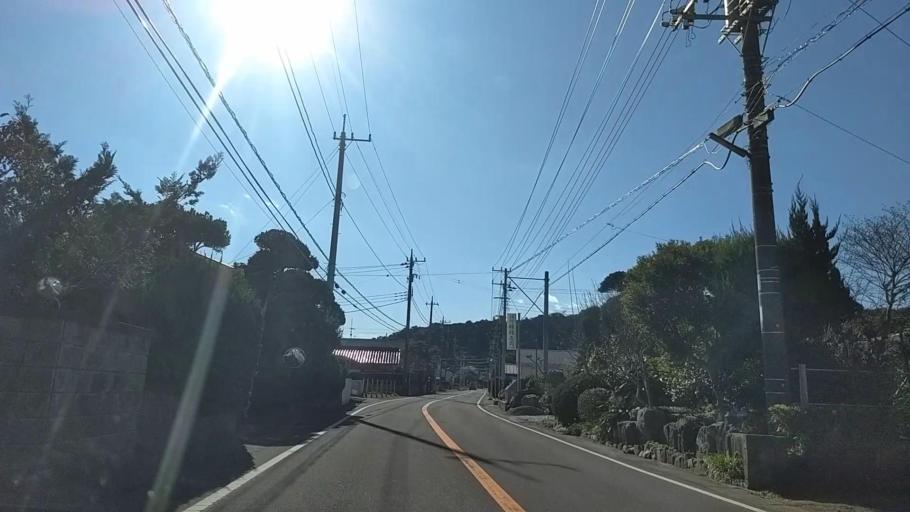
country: JP
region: Chiba
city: Tateyama
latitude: 34.9777
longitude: 139.8634
